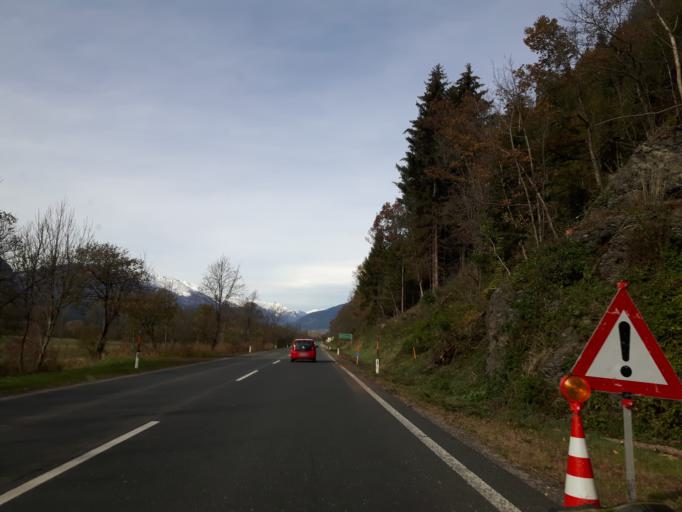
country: AT
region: Tyrol
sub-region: Politischer Bezirk Lienz
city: Lavant
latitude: 46.8051
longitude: 12.8638
